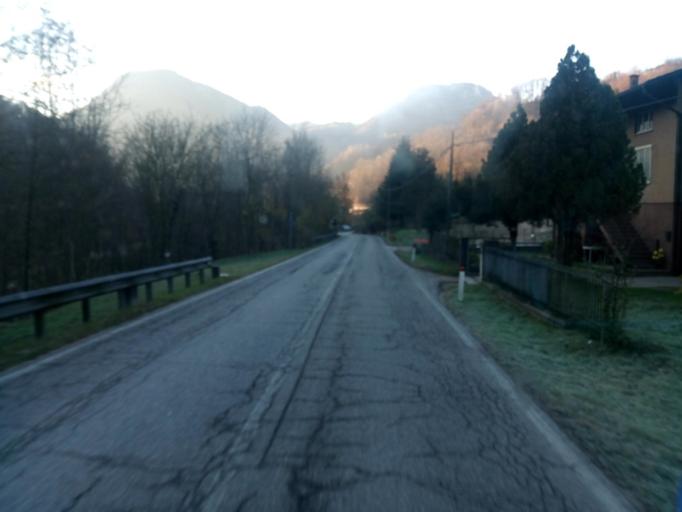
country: IT
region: Veneto
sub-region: Provincia di Vicenza
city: Valli del Pasubio
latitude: 45.7271
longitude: 11.2799
